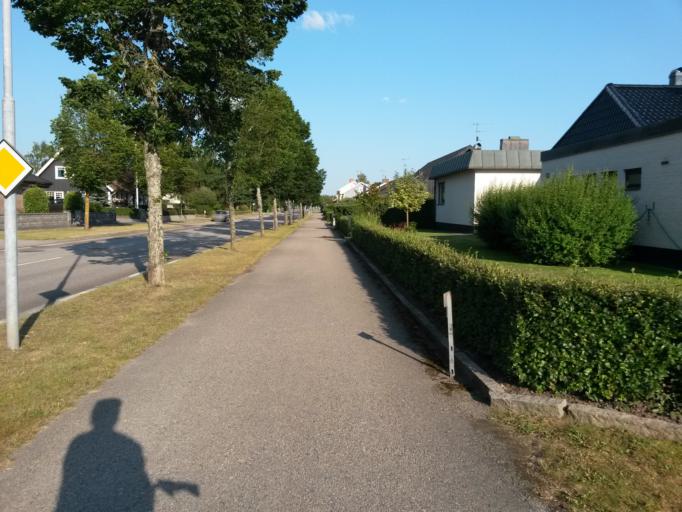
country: SE
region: Vaestra Goetaland
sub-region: Vargarda Kommun
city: Vargarda
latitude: 58.0339
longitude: 12.7975
